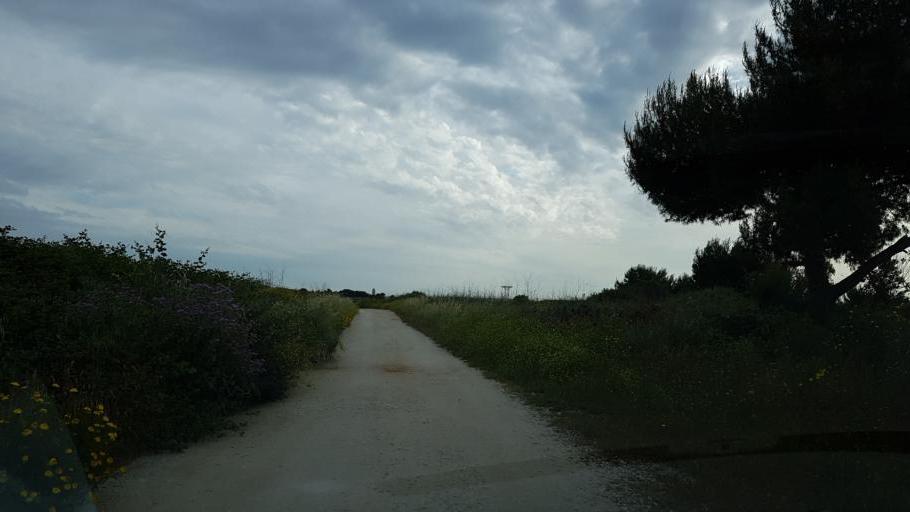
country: IT
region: Apulia
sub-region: Provincia di Brindisi
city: Materdomini
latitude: 40.6575
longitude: 17.9543
